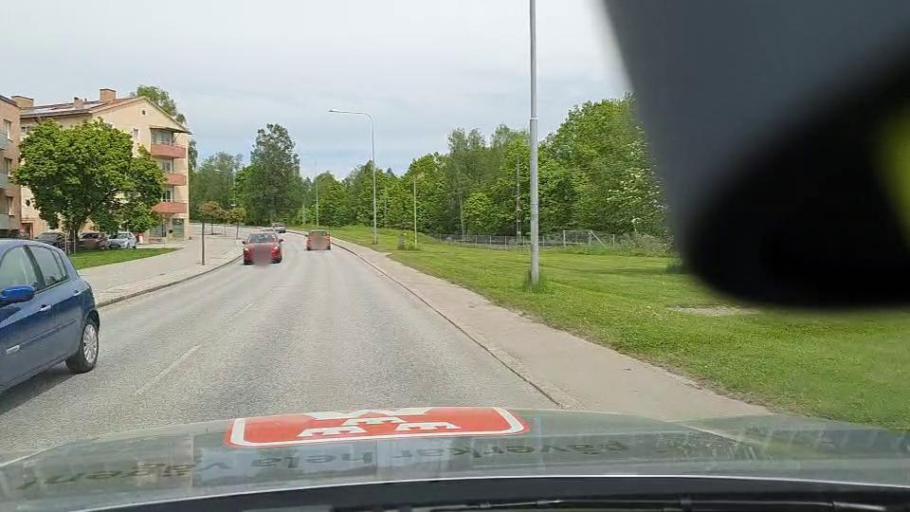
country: SE
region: Soedermanland
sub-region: Flens Kommun
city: Flen
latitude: 59.0542
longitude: 16.5958
